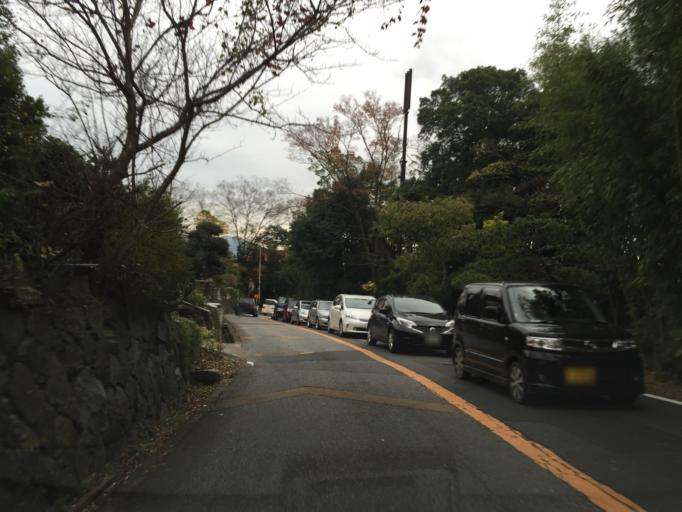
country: JP
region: Ibaraki
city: Tsukuba
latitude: 36.2079
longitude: 140.0842
